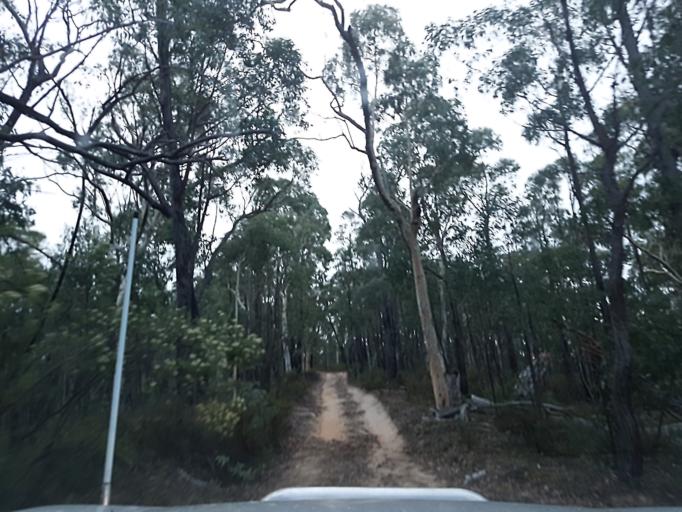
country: AU
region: New South Wales
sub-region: Snowy River
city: Jindabyne
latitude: -36.8596
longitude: 148.2338
